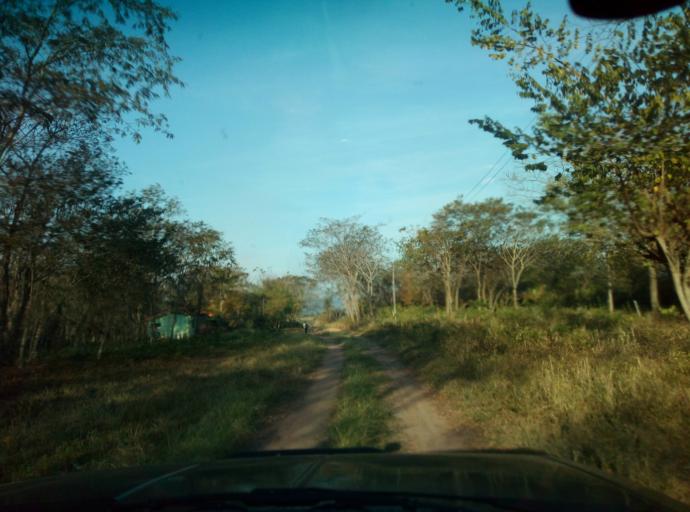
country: PY
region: Caaguazu
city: Doctor Cecilio Baez
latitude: -25.2000
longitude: -56.1319
